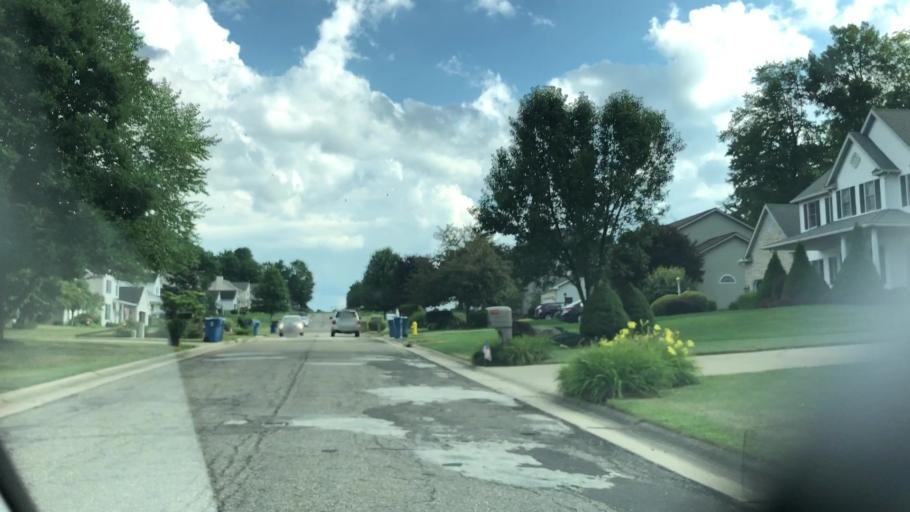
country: US
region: Ohio
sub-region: Summit County
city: Norton
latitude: 41.0337
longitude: -81.6277
